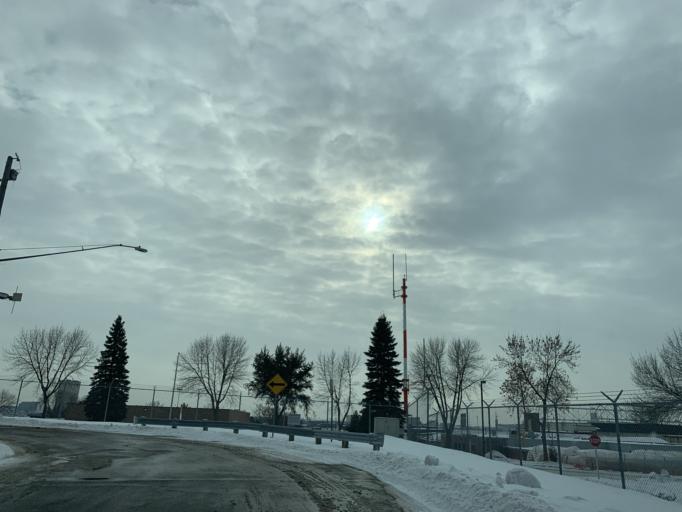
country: US
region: Minnesota
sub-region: Hennepin County
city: Richfield
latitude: 44.8966
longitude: -93.2128
